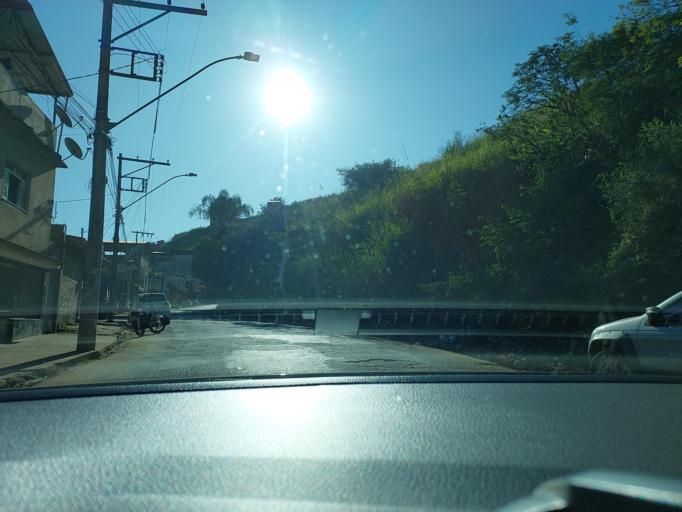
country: BR
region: Minas Gerais
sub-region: Ponte Nova
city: Ponte Nova
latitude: -20.4025
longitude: -42.8970
